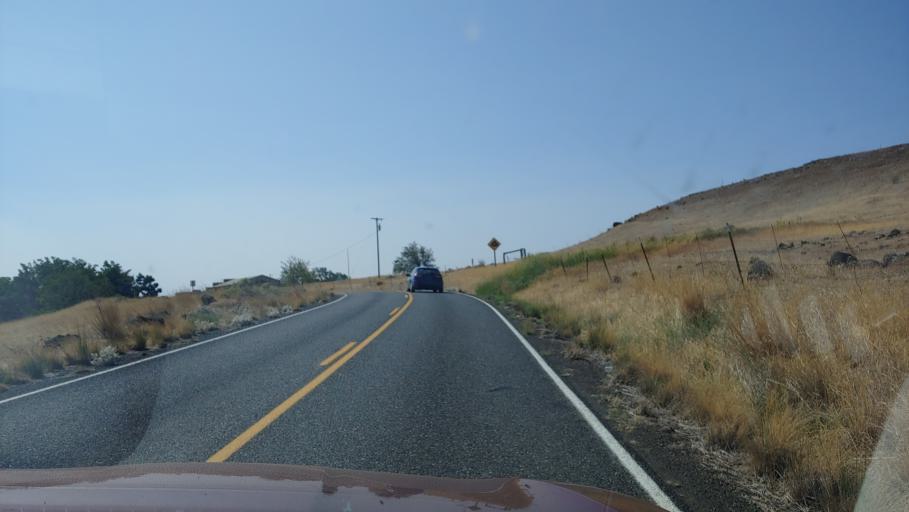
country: US
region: Washington
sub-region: Klickitat County
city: Goldendale
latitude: 45.6972
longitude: -120.8049
